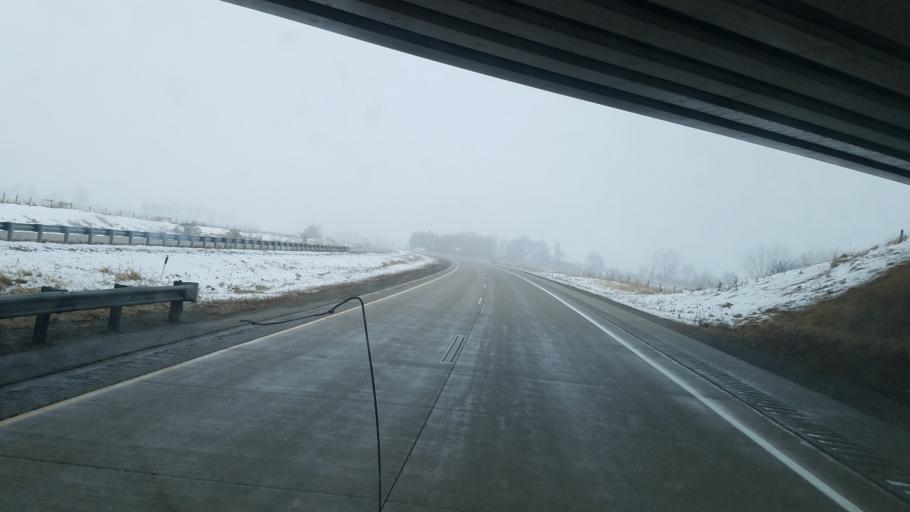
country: US
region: Wisconsin
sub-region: Winnebago County
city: Winneconne
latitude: 44.1016
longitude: -88.6240
